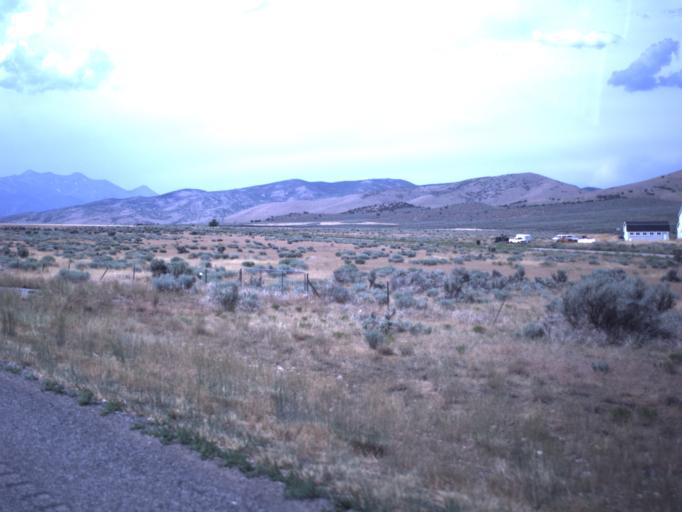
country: US
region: Utah
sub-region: Sanpete County
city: Fountain Green
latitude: 39.6439
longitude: -111.6386
